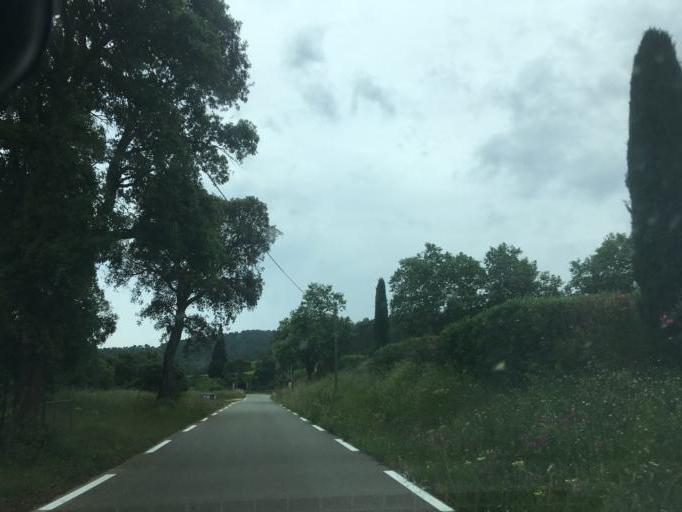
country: FR
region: Provence-Alpes-Cote d'Azur
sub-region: Departement du Var
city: La Londe-les-Maures
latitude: 43.1932
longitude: 6.2091
